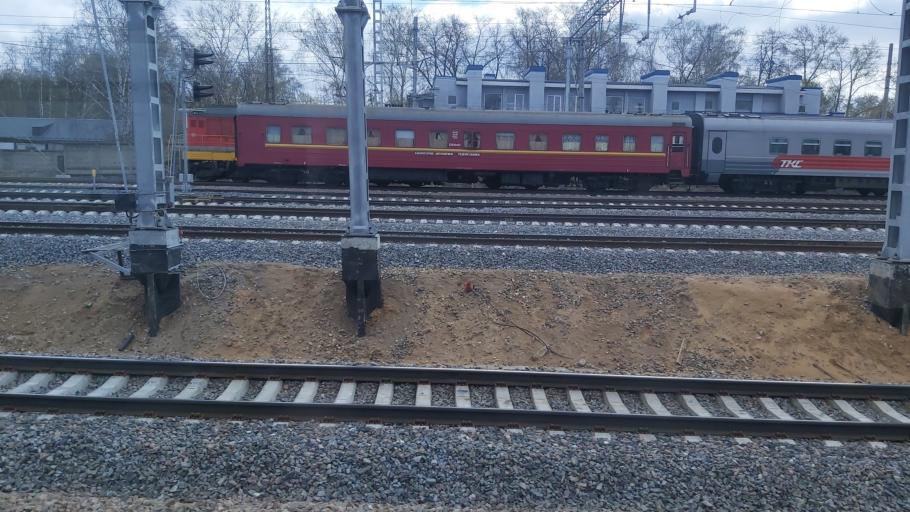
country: RU
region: Moscow
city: Sokol'niki
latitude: 55.7993
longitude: 37.6499
